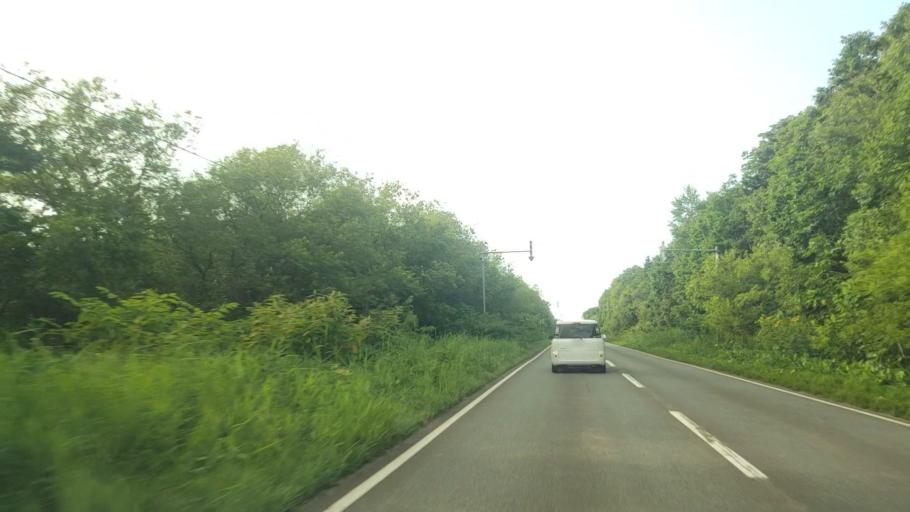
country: JP
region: Hokkaido
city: Makubetsu
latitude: 45.0498
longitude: 141.7513
